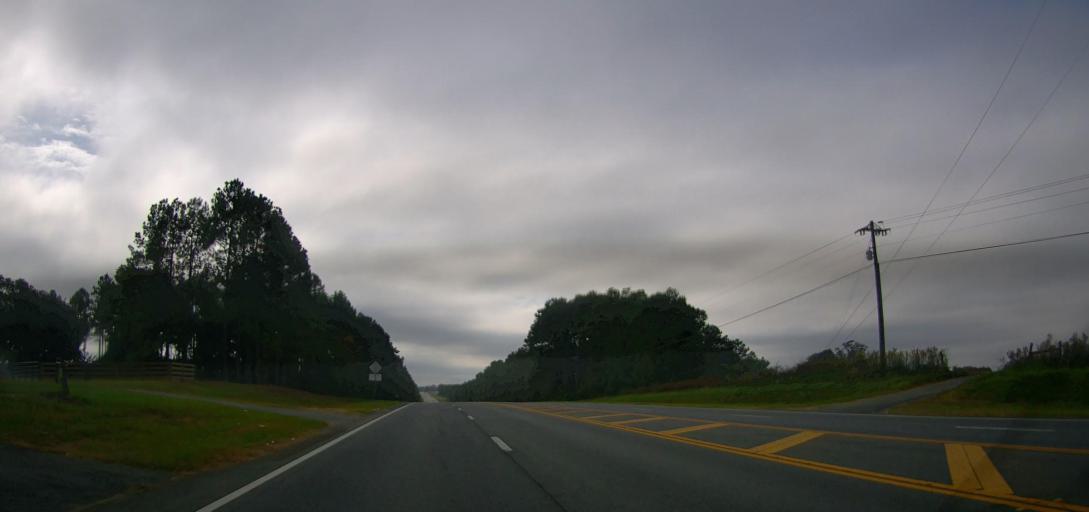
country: US
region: Georgia
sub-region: Tift County
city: Unionville
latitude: 31.3869
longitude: -83.5478
